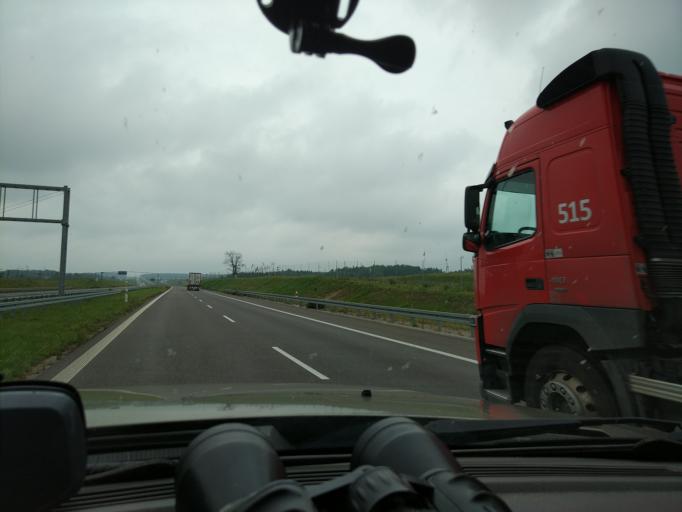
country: PL
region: Podlasie
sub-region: Powiat zambrowski
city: Rutki-Kossaki
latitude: 53.0496
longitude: 22.3781
